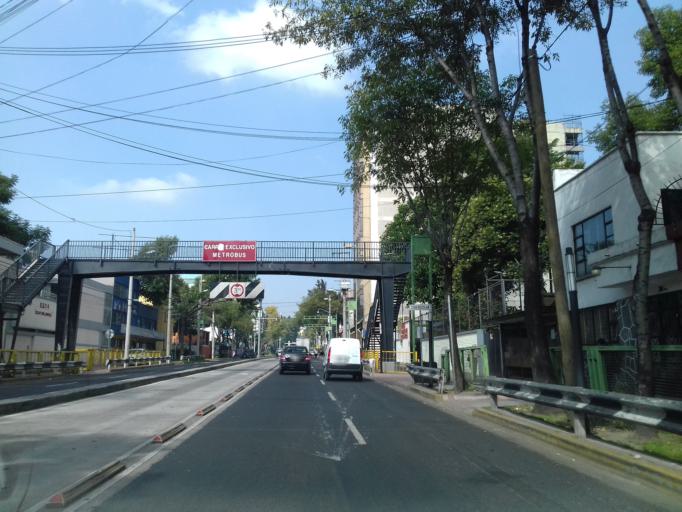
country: MX
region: Mexico City
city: Polanco
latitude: 19.4079
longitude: -99.1865
